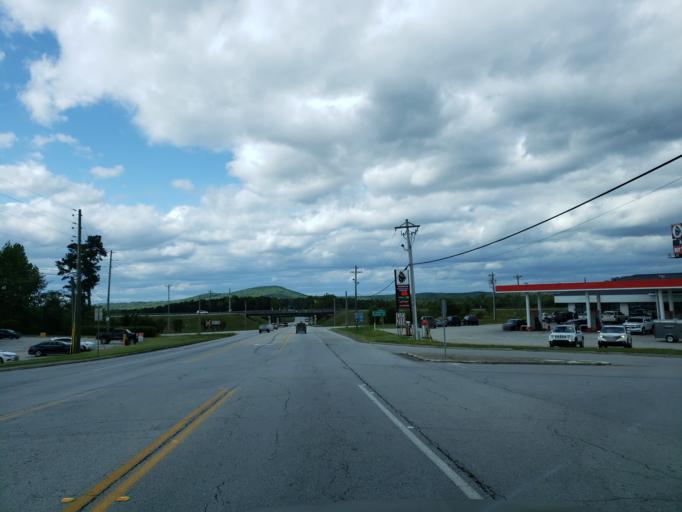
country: US
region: Georgia
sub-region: Haralson County
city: Tallapoosa
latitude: 33.6819
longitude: -85.2625
